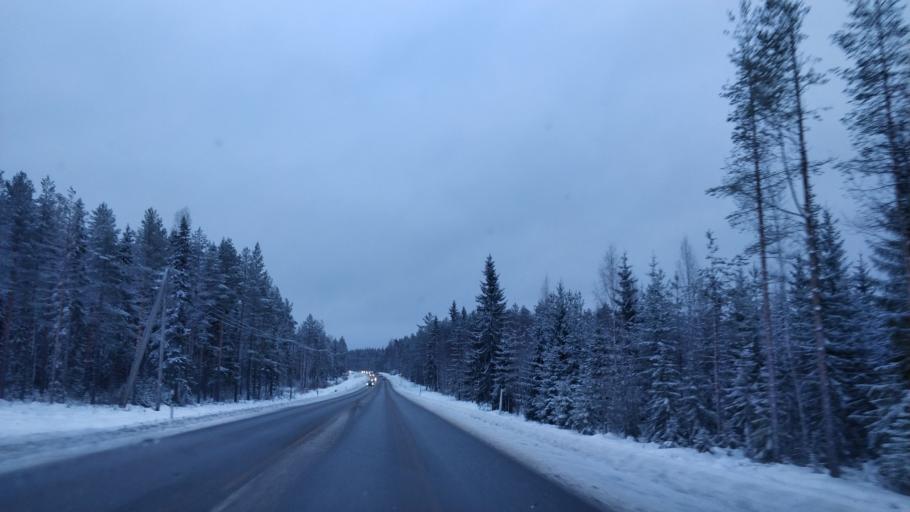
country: FI
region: Central Finland
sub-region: Saarijaervi-Viitasaari
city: Pihtipudas
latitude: 63.2141
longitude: 25.6754
